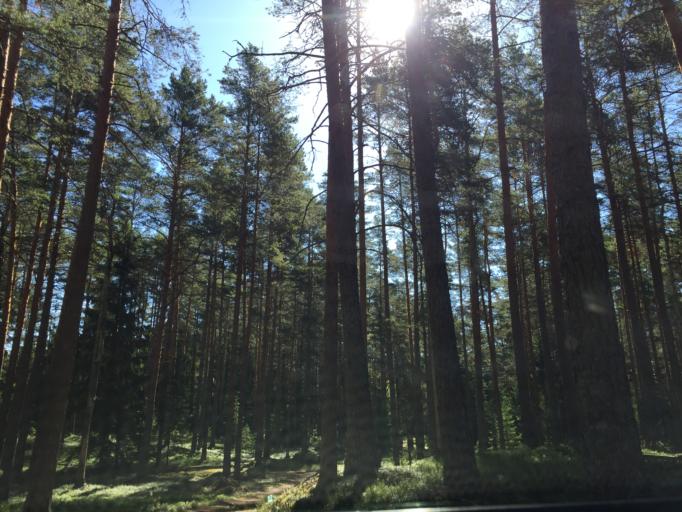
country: LV
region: Ventspils Rajons
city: Piltene
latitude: 57.3201
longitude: 22.0010
